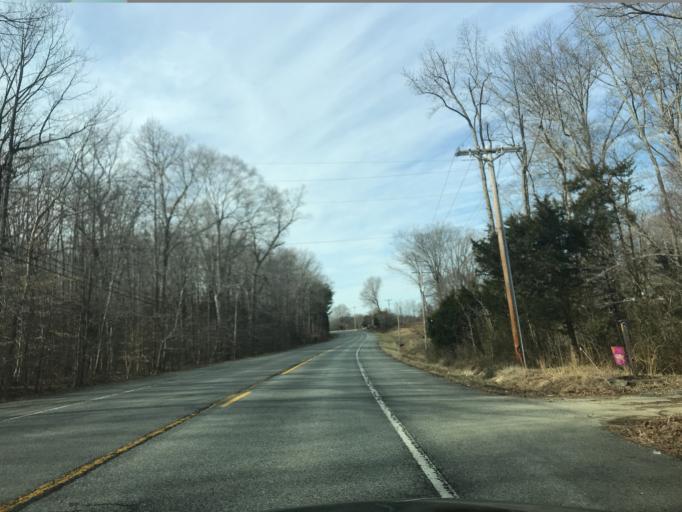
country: US
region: Virginia
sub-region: Prince William County
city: Cherry Hill
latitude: 38.4972
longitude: -77.2163
